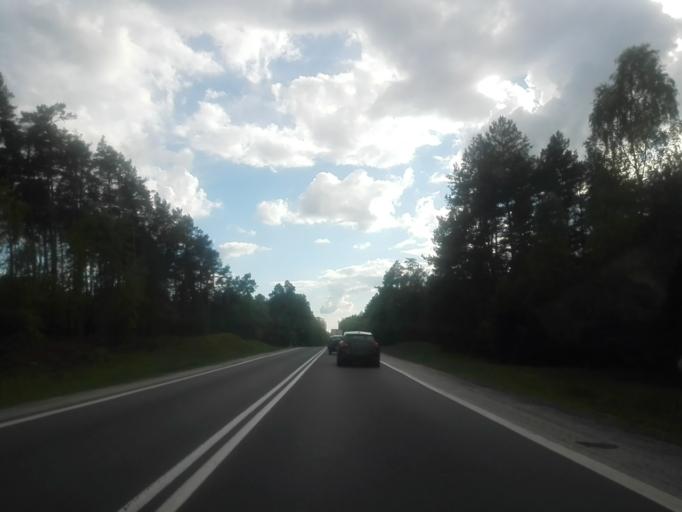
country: PL
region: Masovian Voivodeship
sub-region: Powiat ostrowski
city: Brok
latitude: 52.7268
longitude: 21.7256
